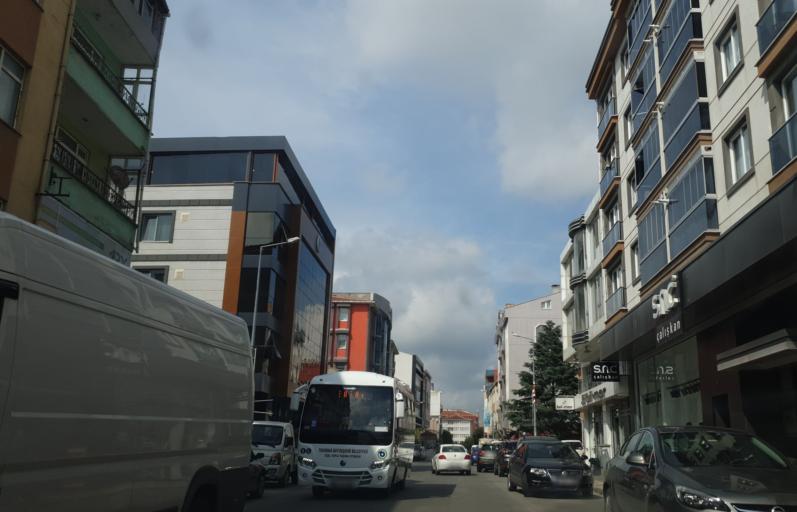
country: TR
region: Tekirdag
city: Saray
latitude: 41.4387
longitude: 27.9180
